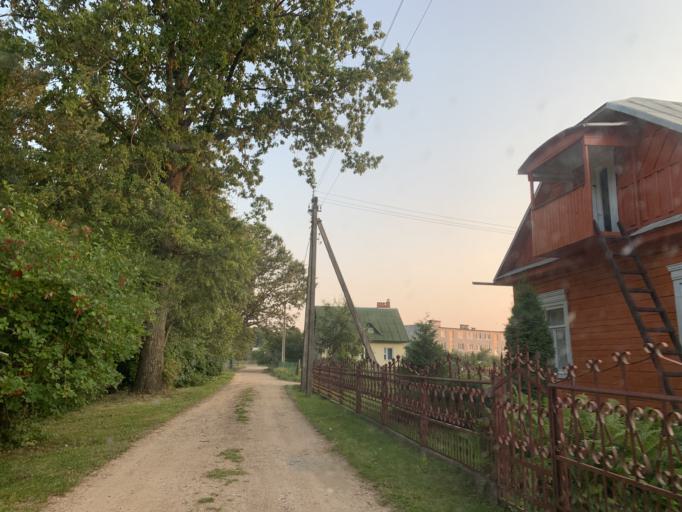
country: BY
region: Minsk
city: Nyasvizh
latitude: 53.2041
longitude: 26.6488
